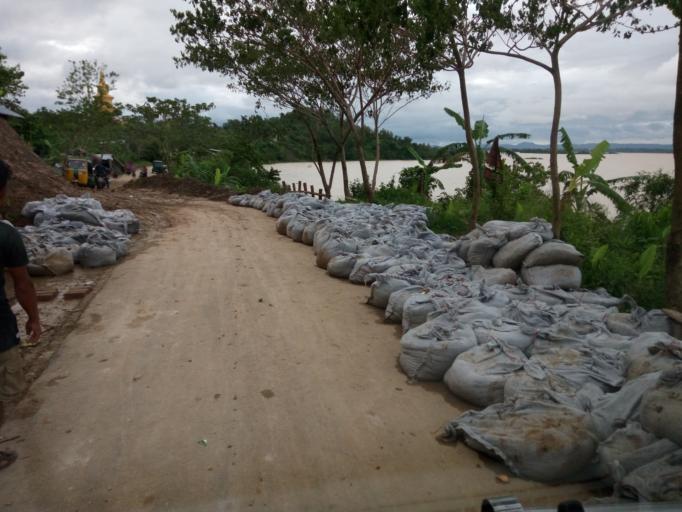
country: BD
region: Chittagong
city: Raojan
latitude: 22.5778
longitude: 92.1748
